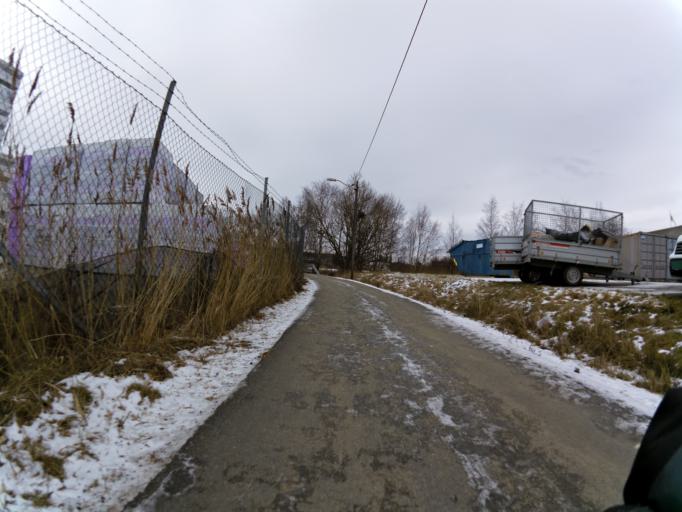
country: NO
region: Ostfold
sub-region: Fredrikstad
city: Fredrikstad
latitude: 59.2072
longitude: 10.8913
